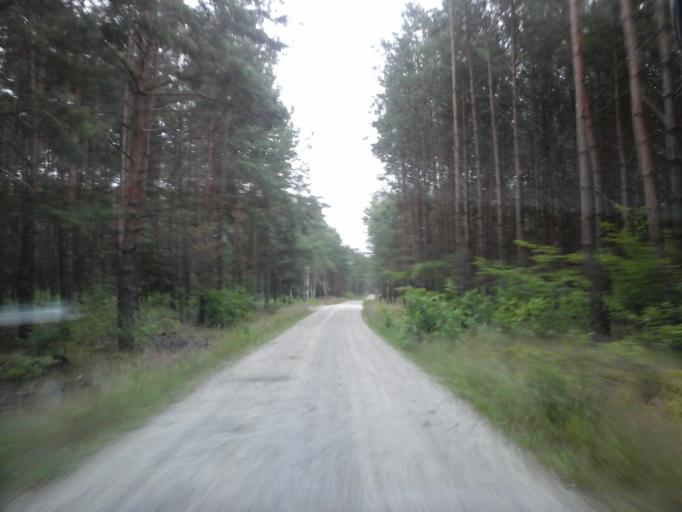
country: PL
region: West Pomeranian Voivodeship
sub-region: Powiat choszczenski
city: Bierzwnik
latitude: 53.0993
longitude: 15.6753
